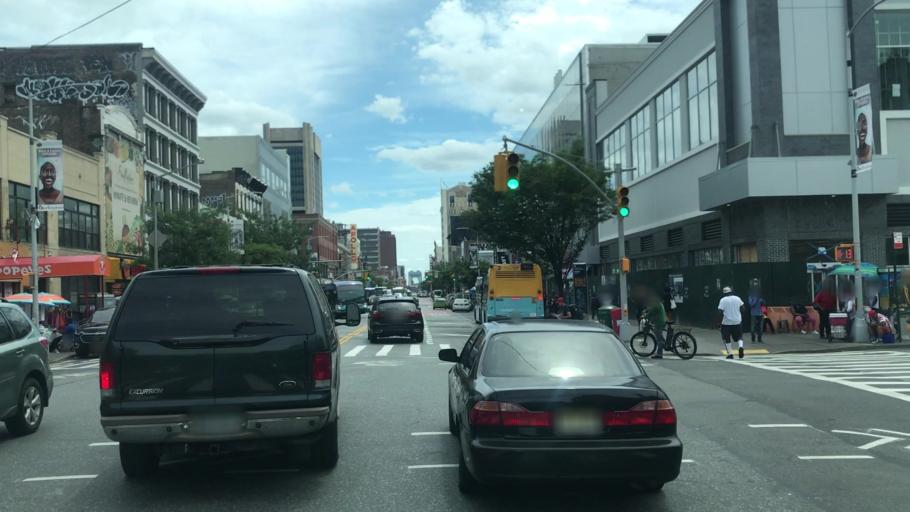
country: US
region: New Jersey
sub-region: Bergen County
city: Edgewater
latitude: 40.8108
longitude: -73.9527
